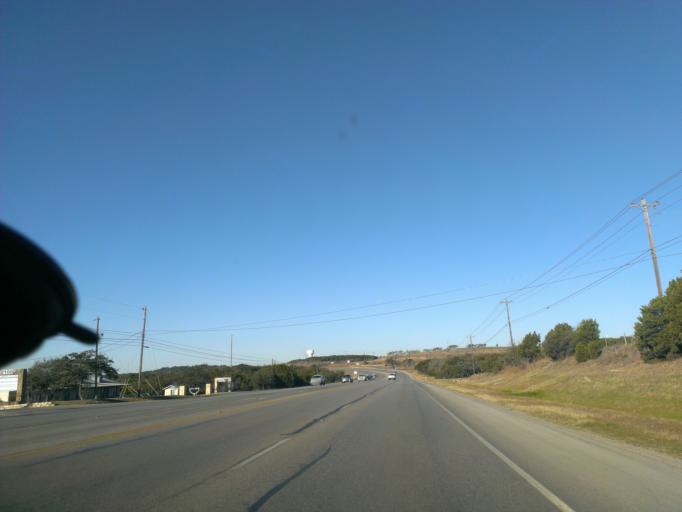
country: US
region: Texas
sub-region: Hays County
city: Dripping Springs
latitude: 30.1953
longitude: -98.0548
